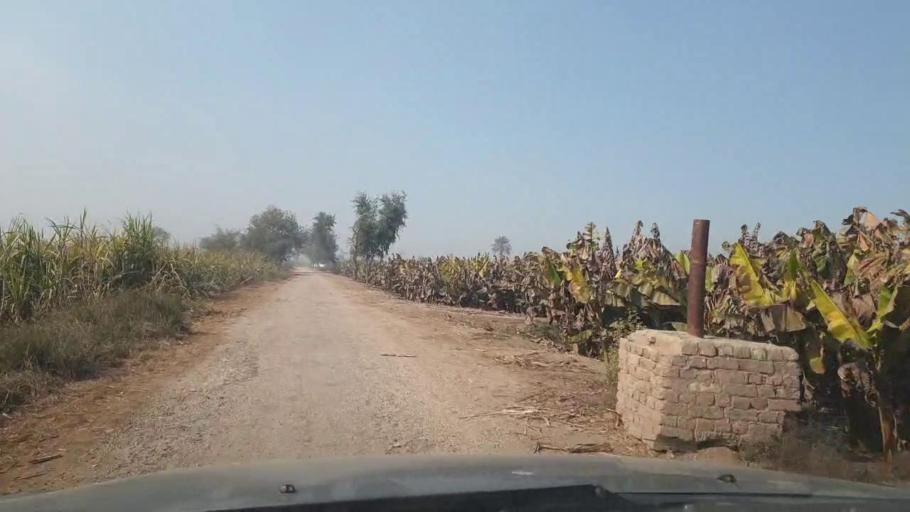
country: PK
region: Sindh
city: Ghotki
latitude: 28.0275
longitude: 69.2540
